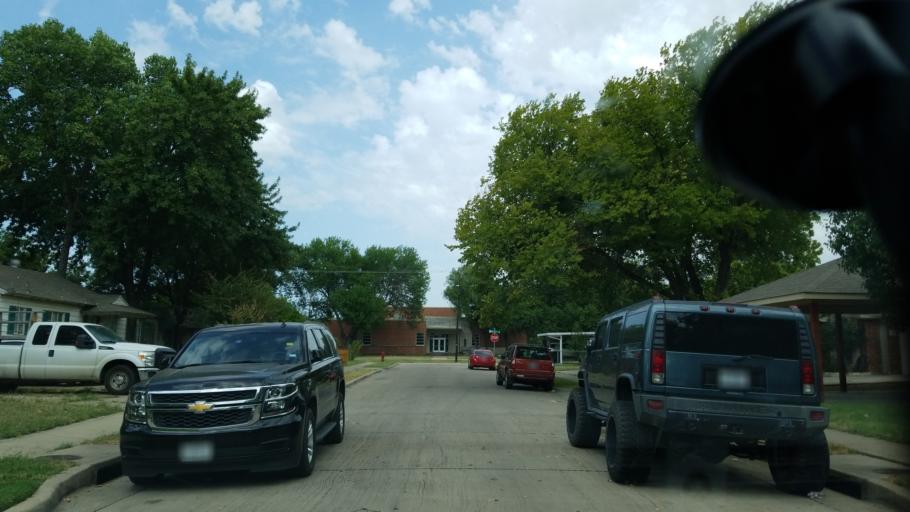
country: US
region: Texas
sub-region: Dallas County
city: Grand Prairie
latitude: 32.7521
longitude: -96.9852
